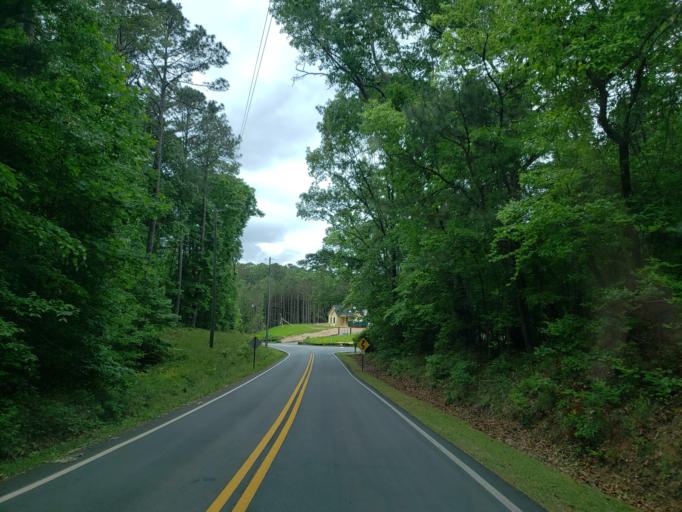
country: US
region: Georgia
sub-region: Bartow County
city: Emerson
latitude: 34.0907
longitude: -84.7651
